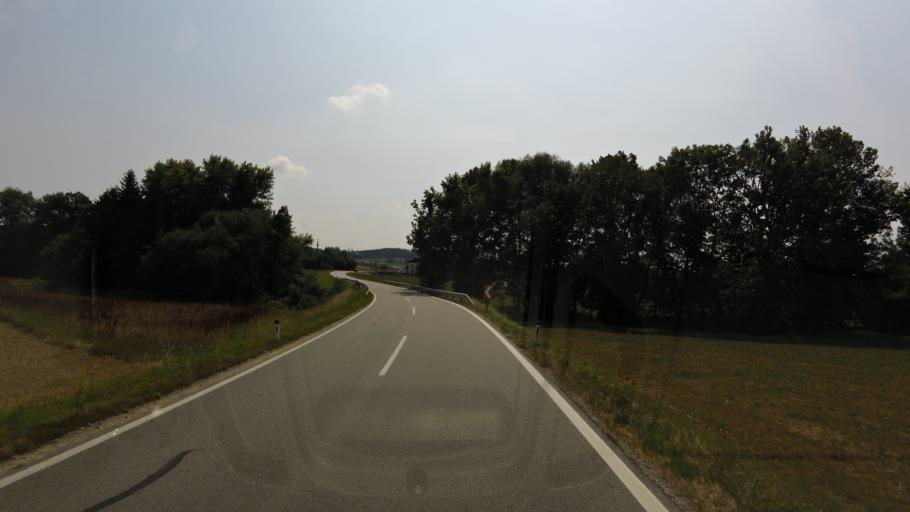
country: DE
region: Bavaria
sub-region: Lower Bavaria
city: Bad Fussing
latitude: 48.2646
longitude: 13.3309
